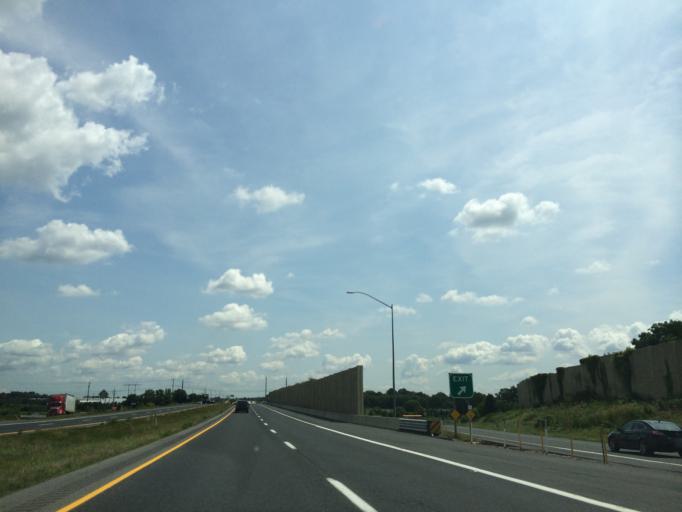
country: US
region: Pennsylvania
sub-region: Lehigh County
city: Trexlertown
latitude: 40.5572
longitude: -75.6123
